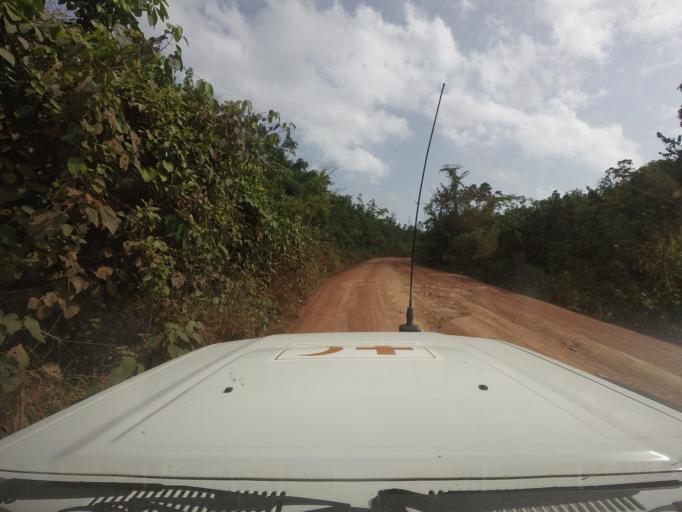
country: LR
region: Bong
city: Gbarnga
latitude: 7.2039
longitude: -9.4448
